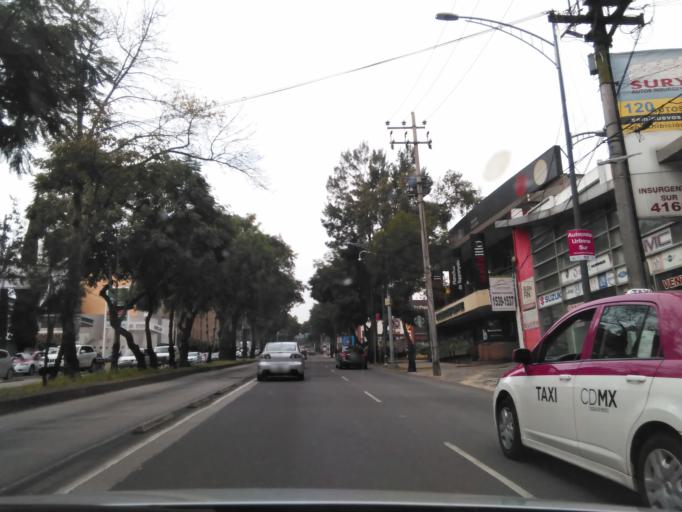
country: MX
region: Mexico City
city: Tlalpan
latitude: 19.2808
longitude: -99.1710
